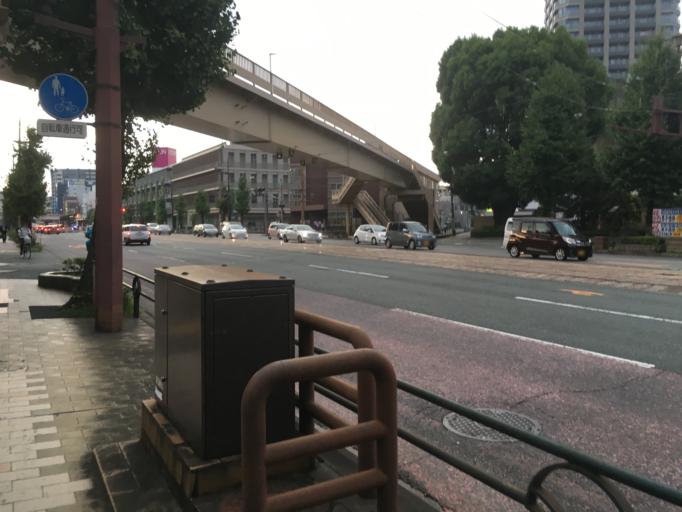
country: JP
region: Kumamoto
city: Kumamoto
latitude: 32.7971
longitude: 130.7205
